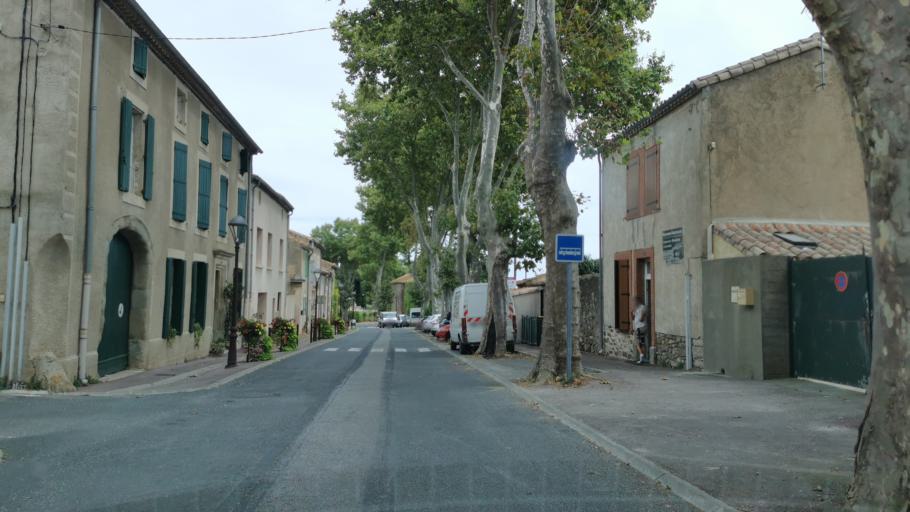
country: FR
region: Languedoc-Roussillon
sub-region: Departement de l'Aude
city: Ginestas
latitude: 43.2680
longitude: 2.8736
